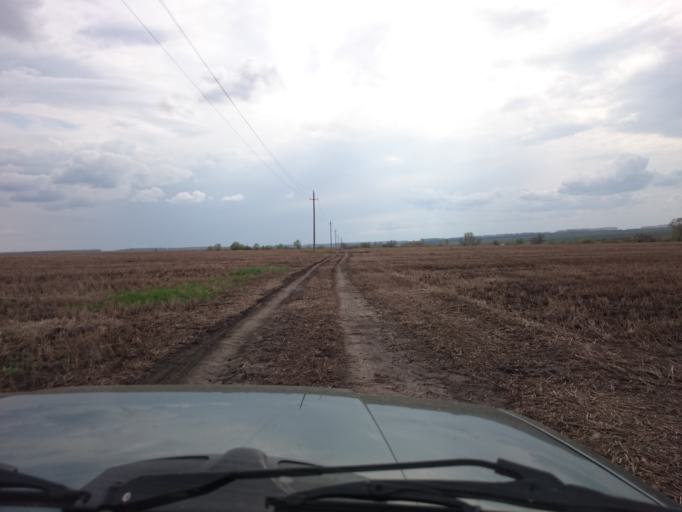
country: RU
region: Mordoviya
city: Kadoshkino
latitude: 54.0191
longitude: 44.4668
